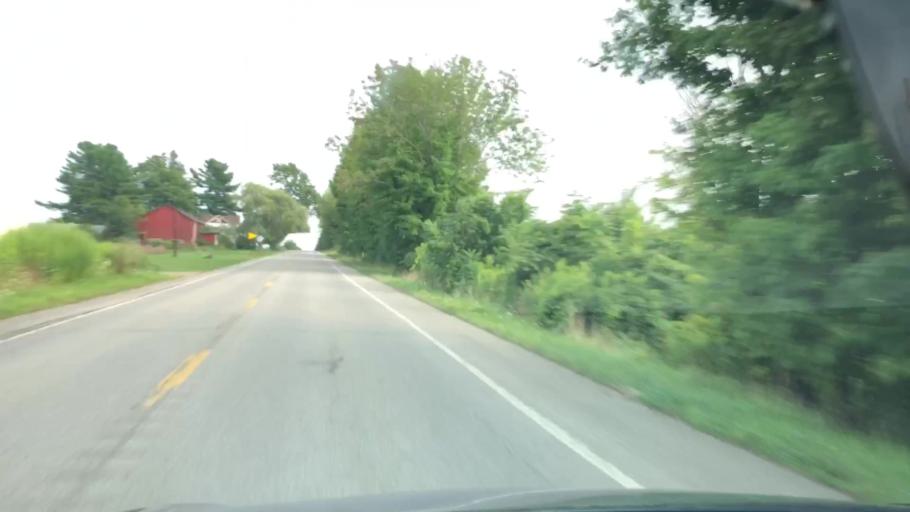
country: US
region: Pennsylvania
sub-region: Erie County
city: Union City
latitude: 41.8116
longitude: -79.8016
